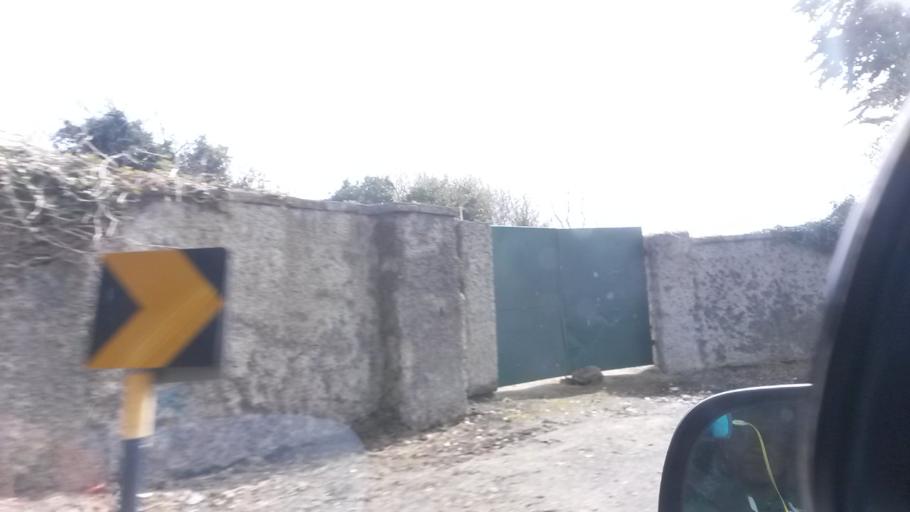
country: IE
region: Leinster
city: Portmarnock
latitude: 53.4288
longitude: -6.1522
